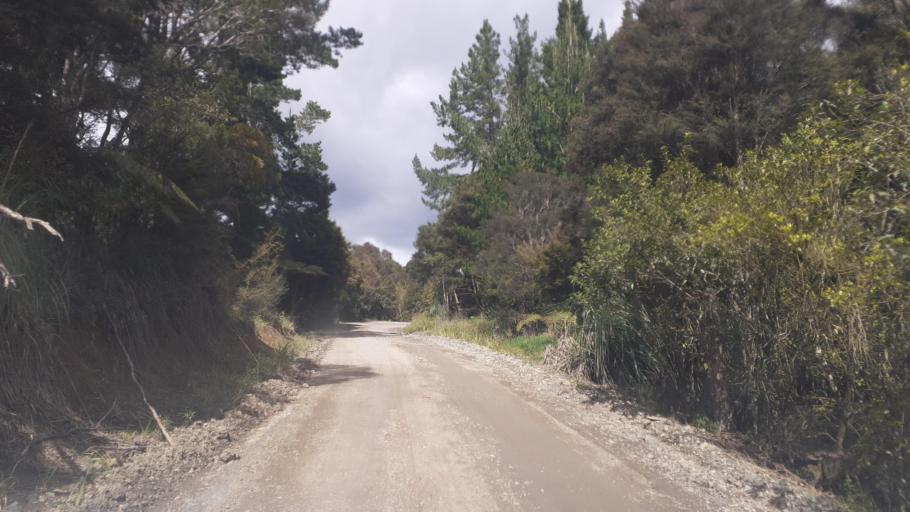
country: NZ
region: Northland
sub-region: Far North District
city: Moerewa
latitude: -35.5801
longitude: 173.9424
